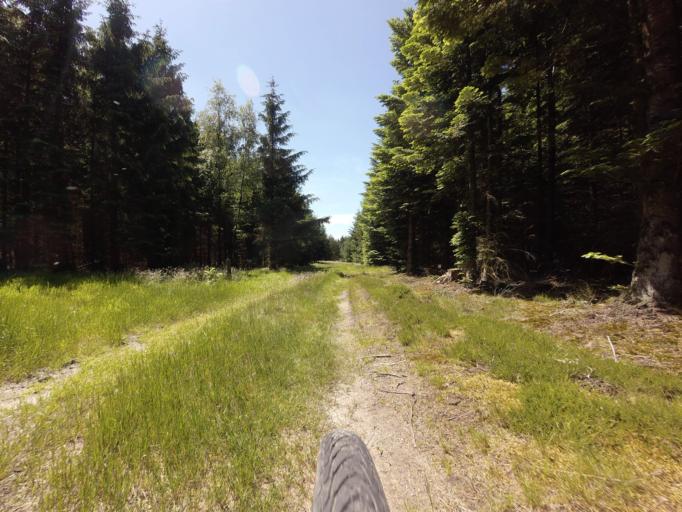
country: DK
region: Central Jutland
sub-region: Silkeborg Kommune
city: Virklund
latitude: 56.0564
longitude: 9.4791
